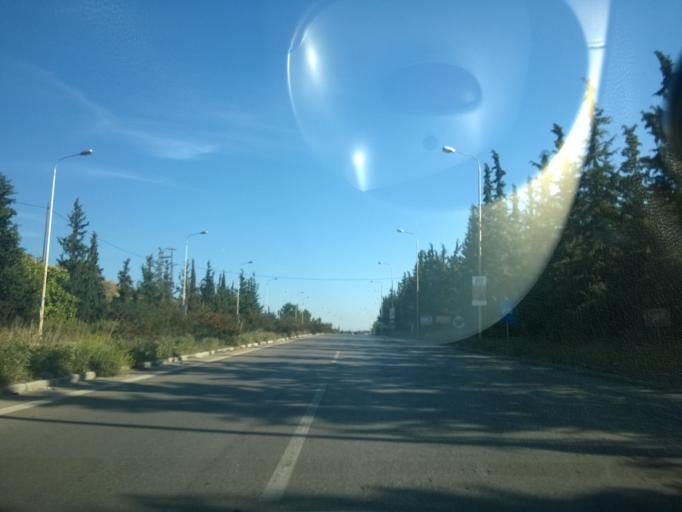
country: GR
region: Central Macedonia
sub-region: Nomos Thessalonikis
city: Kardia
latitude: 40.4569
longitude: 23.0030
